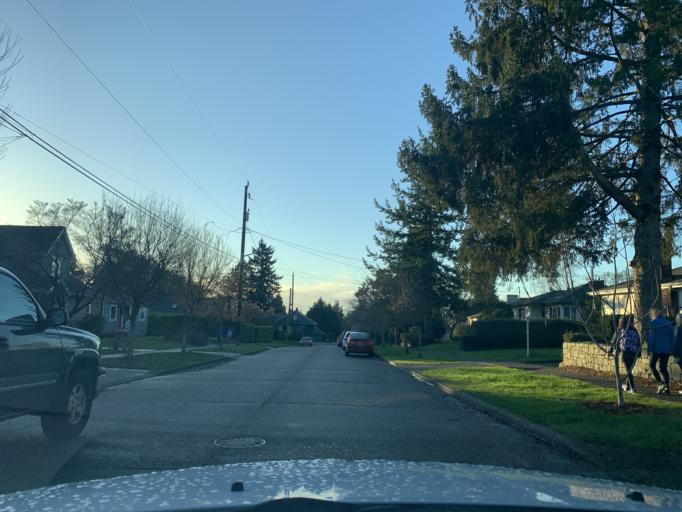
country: US
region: Washington
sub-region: King County
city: Shoreline
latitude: 47.6923
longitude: -122.3244
